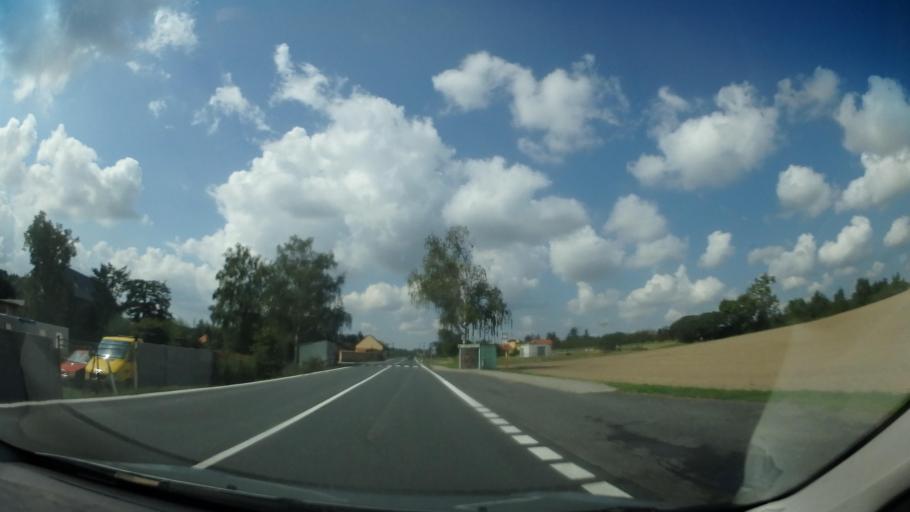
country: CZ
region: Central Bohemia
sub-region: Okres Kolin
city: Kourim
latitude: 49.9660
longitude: 14.9821
